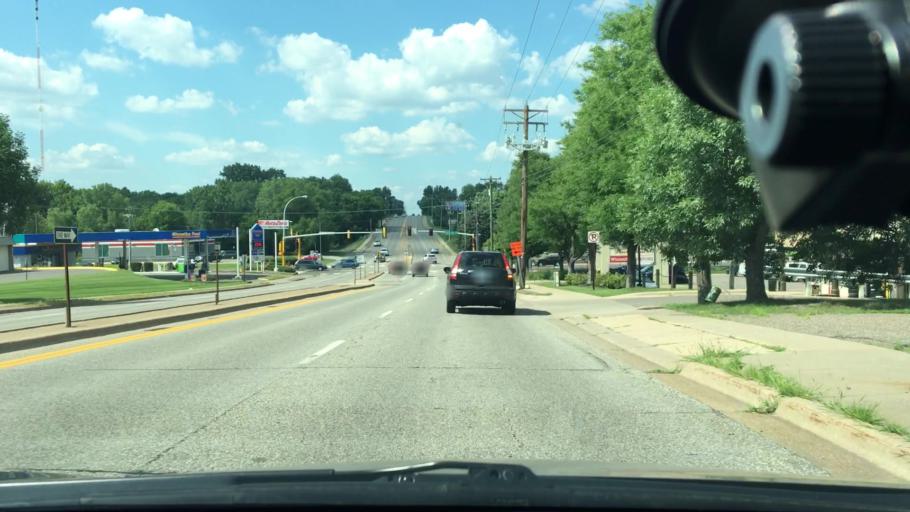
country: US
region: Minnesota
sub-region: Hennepin County
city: New Hope
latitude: 45.0207
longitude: -93.3802
